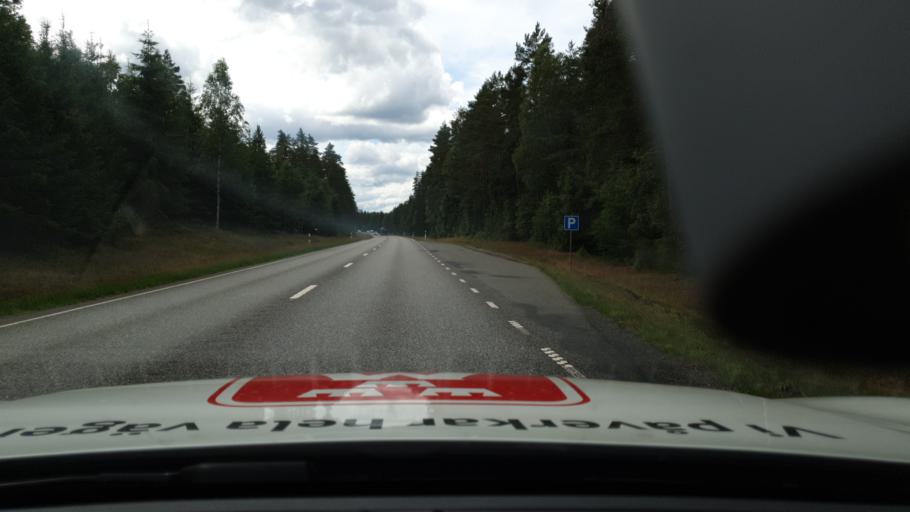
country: SE
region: Joenkoeping
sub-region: Mullsjo Kommun
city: Mullsjoe
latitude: 57.7401
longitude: 13.8826
